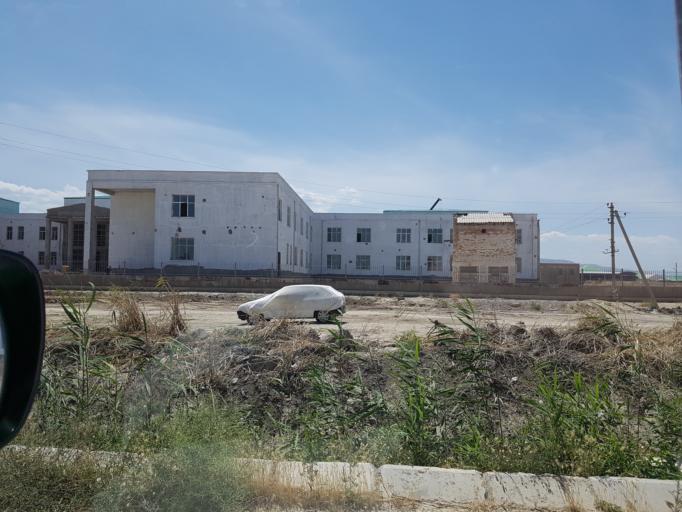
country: TM
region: Ahal
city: Abadan
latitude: 38.1707
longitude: 57.9588
